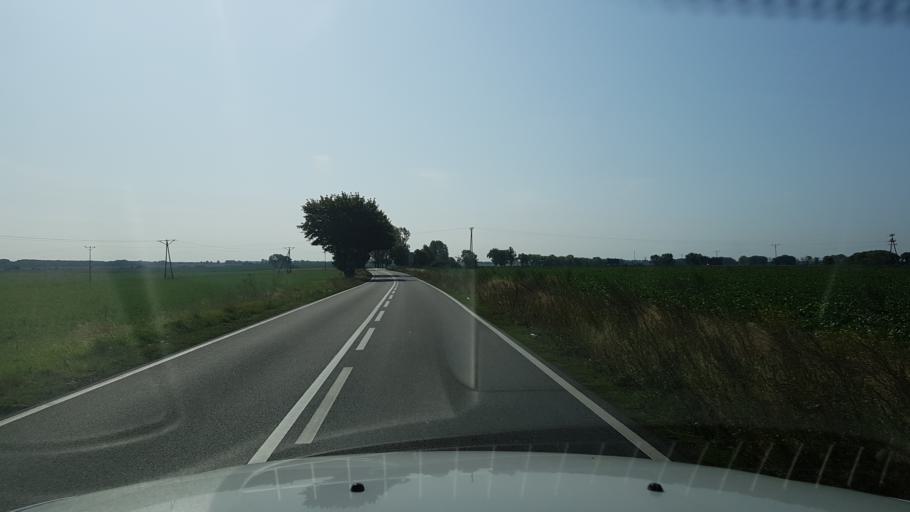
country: PL
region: West Pomeranian Voivodeship
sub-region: Powiat stargardzki
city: Stargard Szczecinski
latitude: 53.2650
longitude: 15.0925
